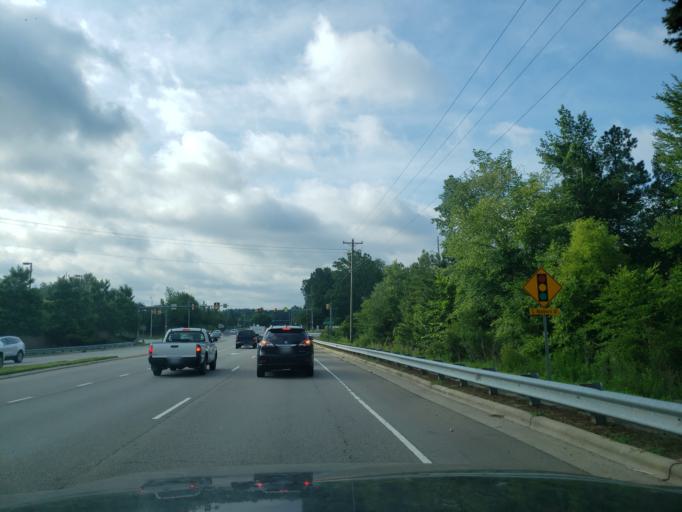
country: US
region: North Carolina
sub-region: Durham County
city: Durham
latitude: 35.9487
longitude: -78.9249
